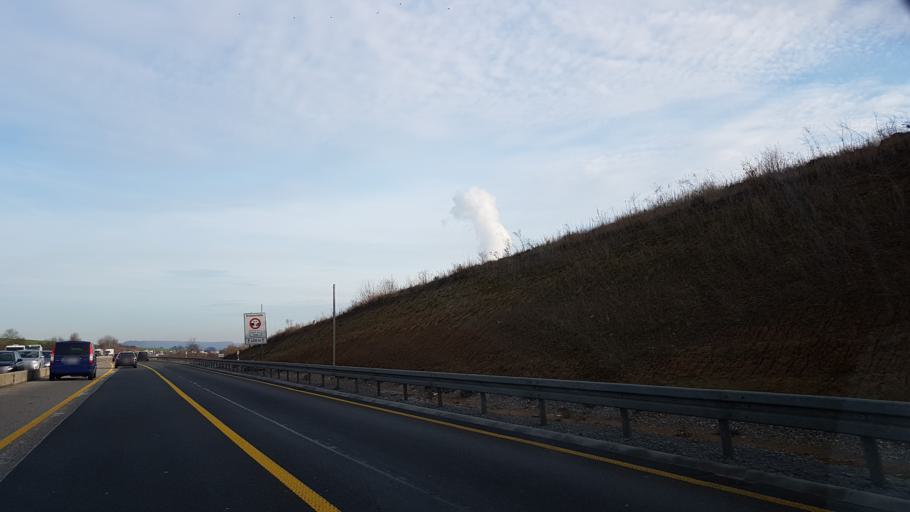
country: DE
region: Baden-Wuerttemberg
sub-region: Regierungsbezirk Stuttgart
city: Bad Wimpfen
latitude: 49.1886
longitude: 9.1656
